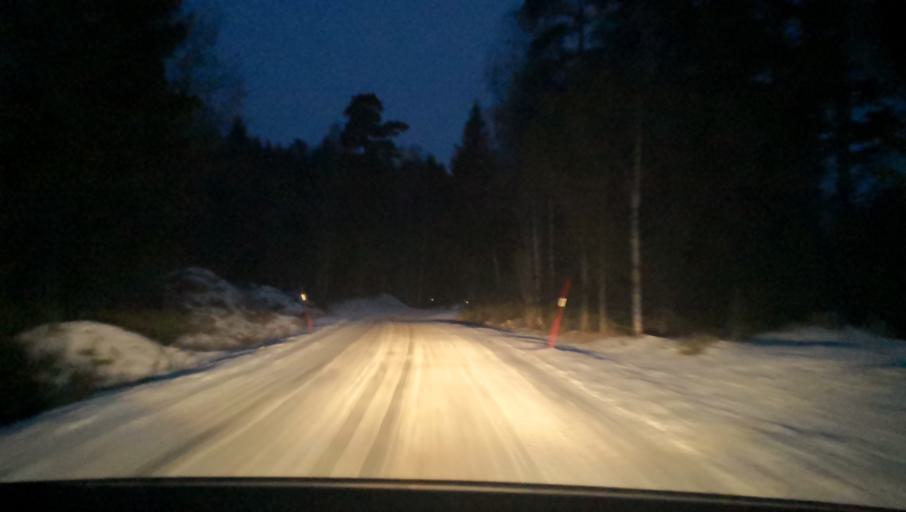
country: SE
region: Uppsala
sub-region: Heby Kommun
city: Tarnsjo
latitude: 60.2604
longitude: 16.7808
